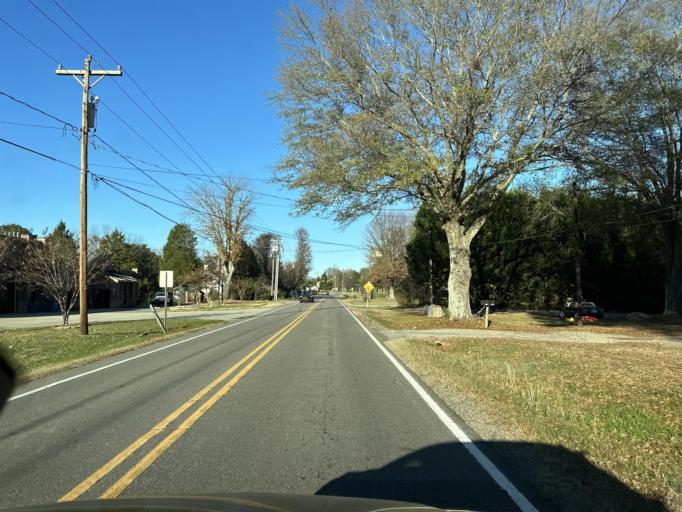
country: US
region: North Carolina
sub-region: Catawba County
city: Claremont
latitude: 35.6406
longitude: -81.0912
